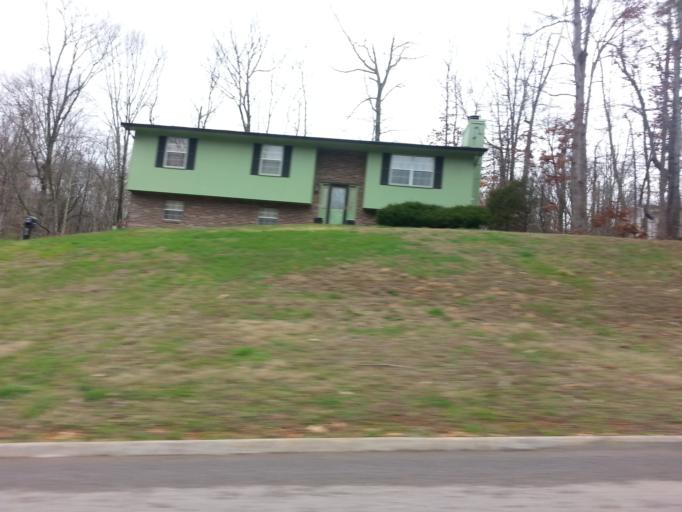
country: US
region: Tennessee
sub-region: Knox County
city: Knoxville
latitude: 35.9910
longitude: -84.0163
